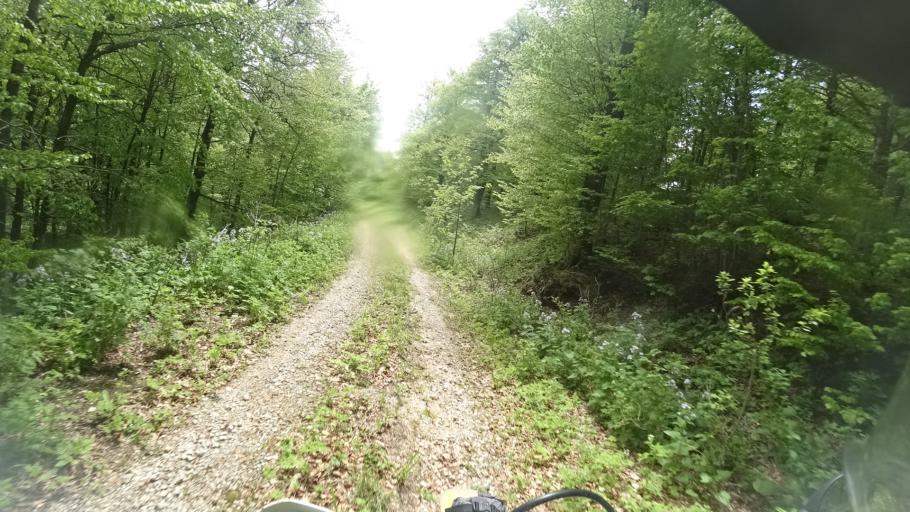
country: BA
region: Federation of Bosnia and Herzegovina
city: Orasac
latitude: 44.5690
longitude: 15.8789
